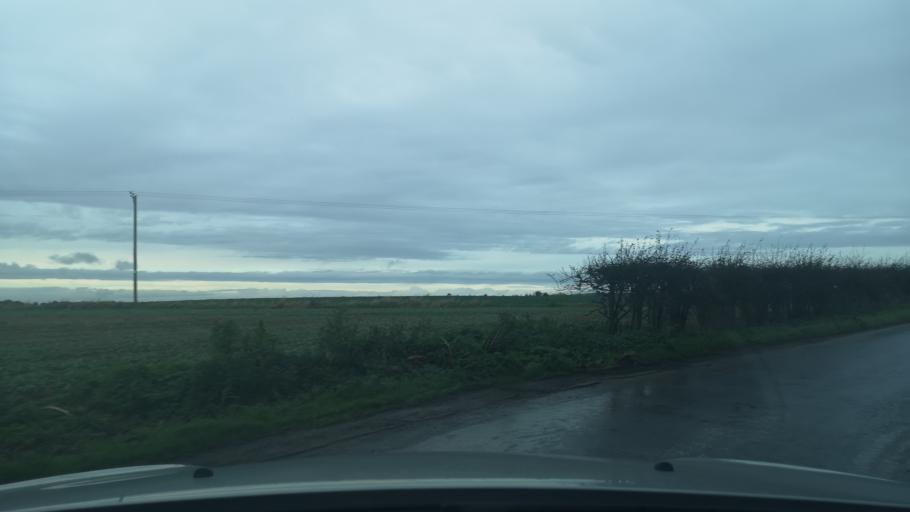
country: GB
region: England
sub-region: East Riding of Yorkshire
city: Holmpton
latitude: 53.6766
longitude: 0.0926
